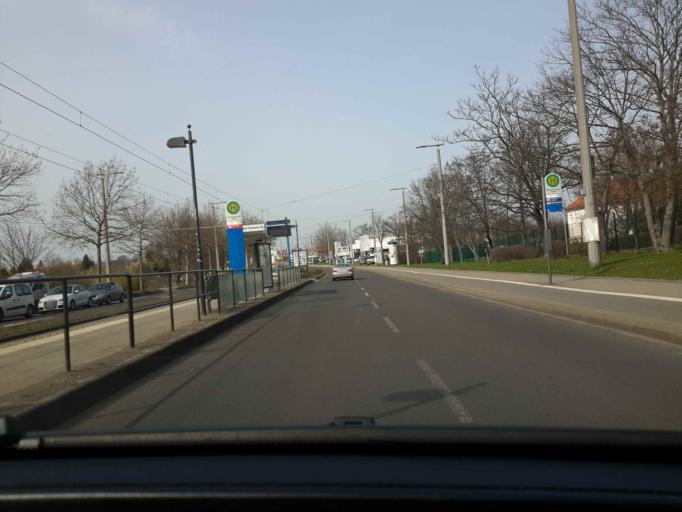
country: DE
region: Saxony
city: Leipzig
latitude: 51.3763
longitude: 12.3855
